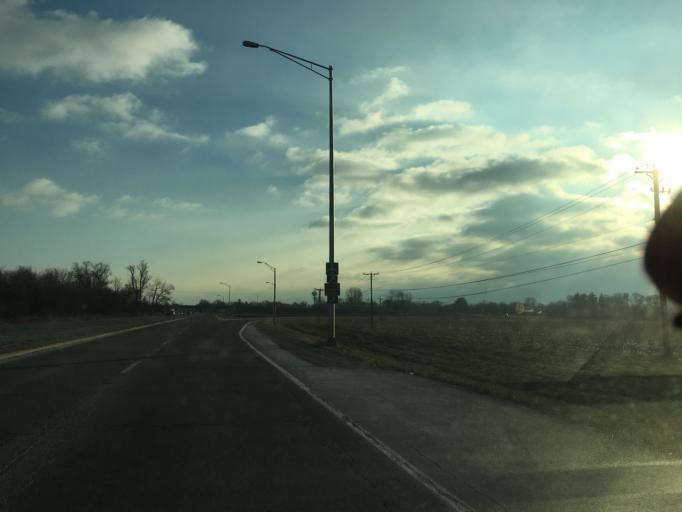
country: US
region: Illinois
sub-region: Kane County
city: Sugar Grove
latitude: 41.7698
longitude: -88.4427
